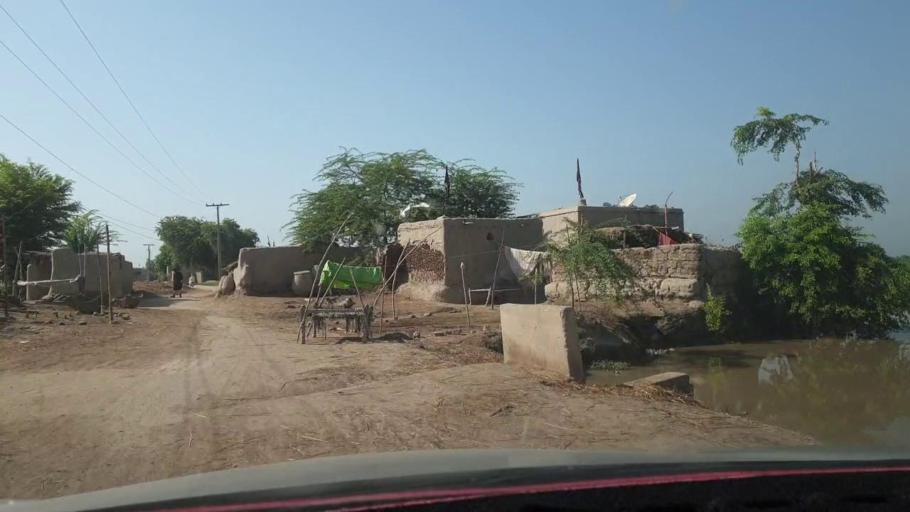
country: PK
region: Sindh
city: Nasirabad
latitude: 27.3808
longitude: 67.8817
